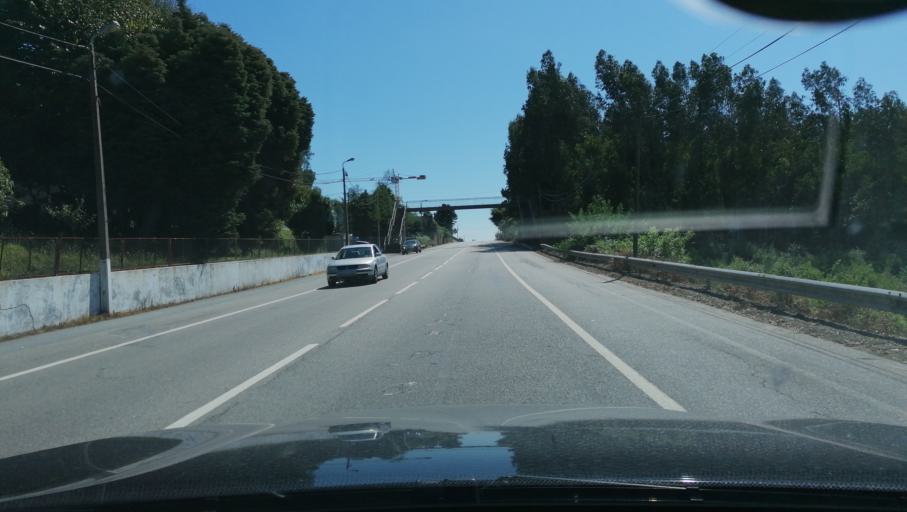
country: PT
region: Porto
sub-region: Vila Nova de Gaia
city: Gulpilhares
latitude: 41.0814
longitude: -8.6358
